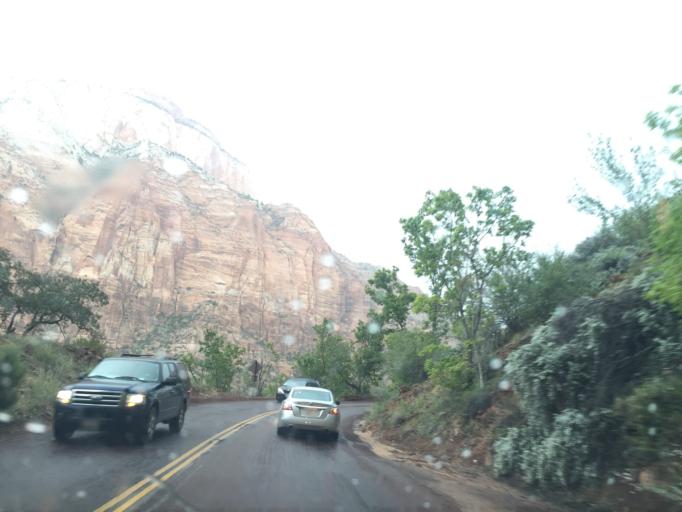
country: US
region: Utah
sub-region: Washington County
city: Hildale
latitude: 37.2123
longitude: -112.9634
